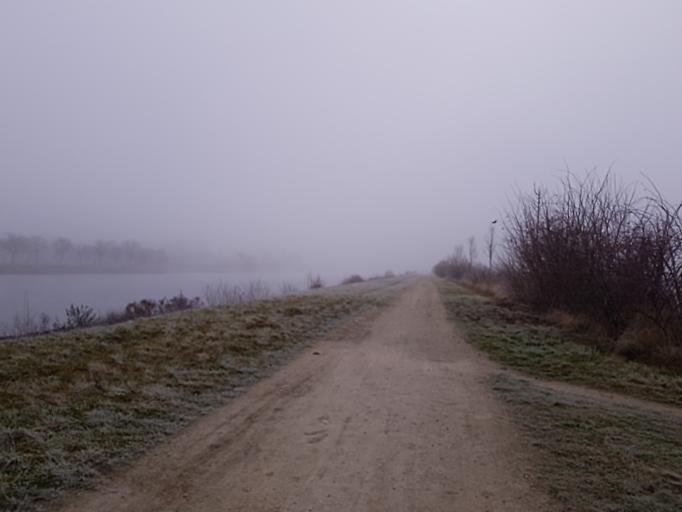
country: BE
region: Flanders
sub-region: Provincie Vlaams-Brabant
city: Grimbergen
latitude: 50.9670
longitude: 4.3982
